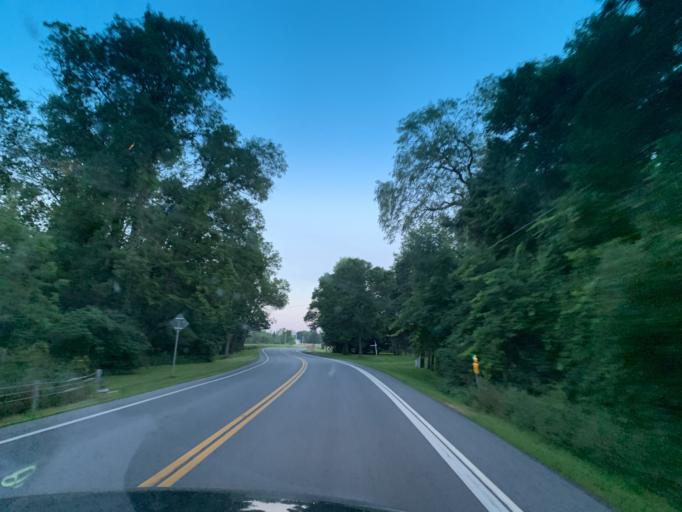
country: US
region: New York
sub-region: Chenango County
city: New Berlin
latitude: 42.7435
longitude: -75.2966
